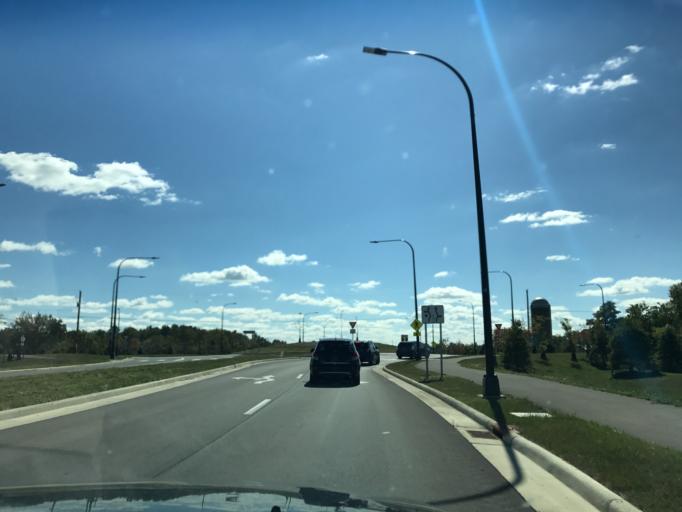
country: US
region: Ohio
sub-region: Delaware County
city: Delaware
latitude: 40.2455
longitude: -83.0935
